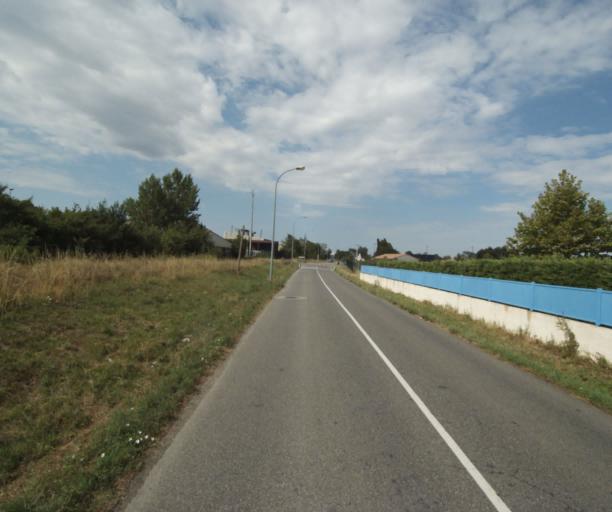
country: FR
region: Midi-Pyrenees
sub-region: Departement de la Haute-Garonne
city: Revel
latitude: 43.4554
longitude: 1.9917
